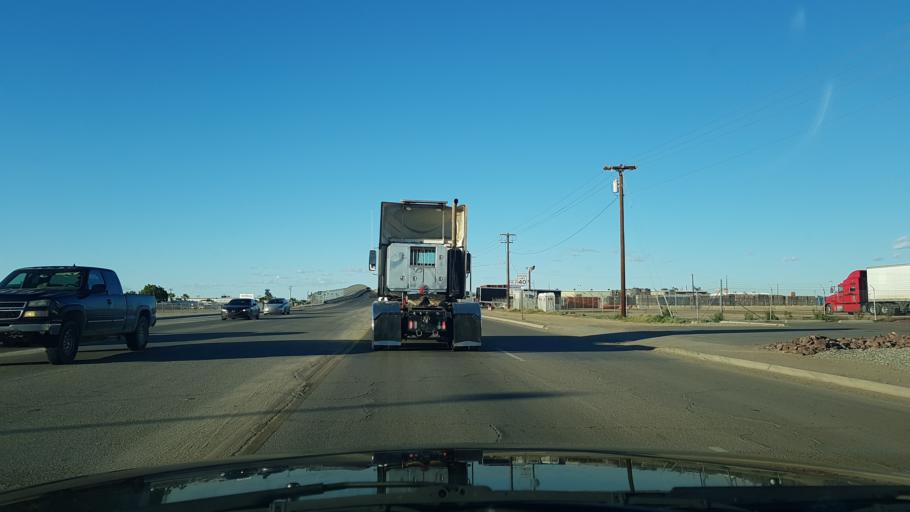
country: US
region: Arizona
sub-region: Yuma County
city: Yuma
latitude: 32.6845
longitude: -114.5988
